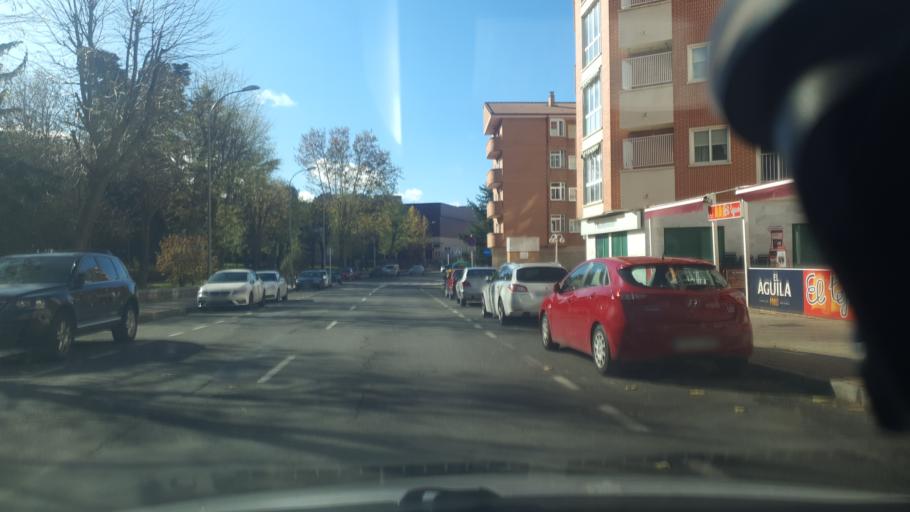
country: ES
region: Castille and Leon
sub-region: Provincia de Avila
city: Avila
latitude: 40.6589
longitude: -4.6871
